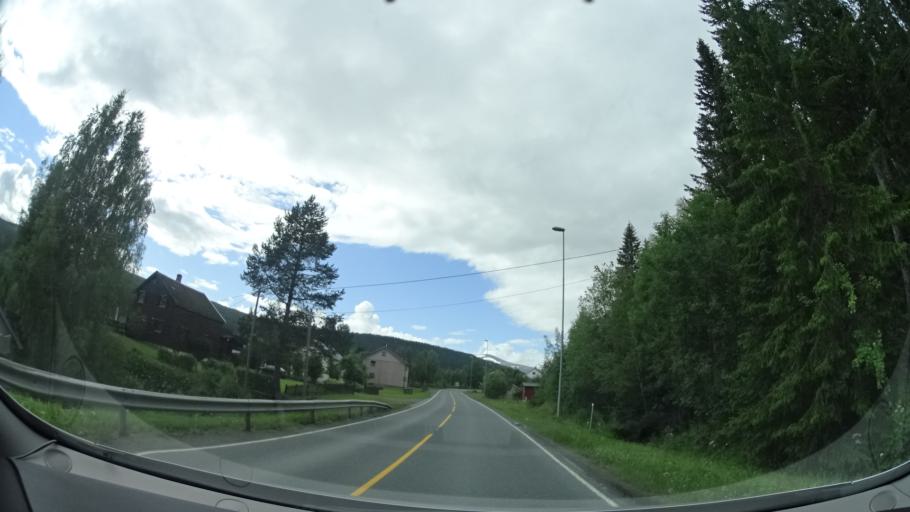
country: NO
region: Nord-Trondelag
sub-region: Meraker
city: Meraker
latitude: 63.3977
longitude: 11.7916
